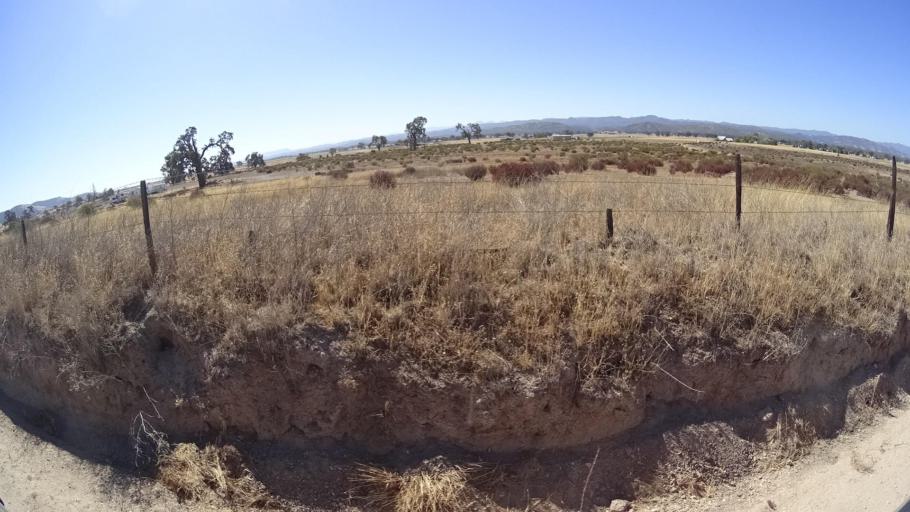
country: US
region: California
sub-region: Monterey County
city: King City
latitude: 35.9515
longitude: -121.0699
